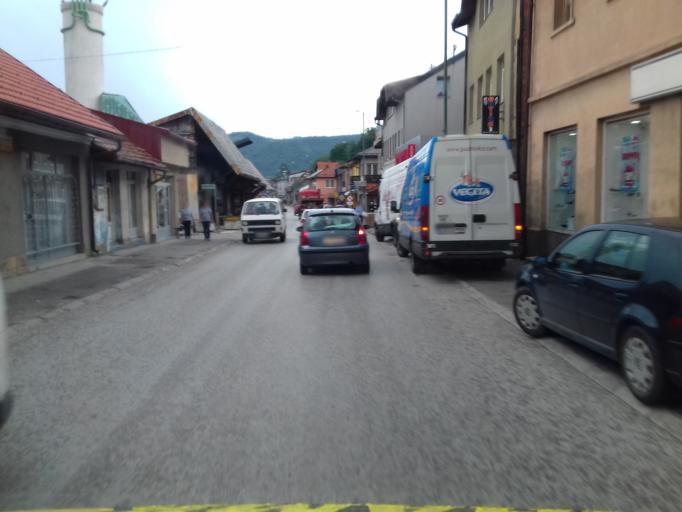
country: BA
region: Federation of Bosnia and Herzegovina
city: Visoko
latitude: 43.9855
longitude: 18.1796
